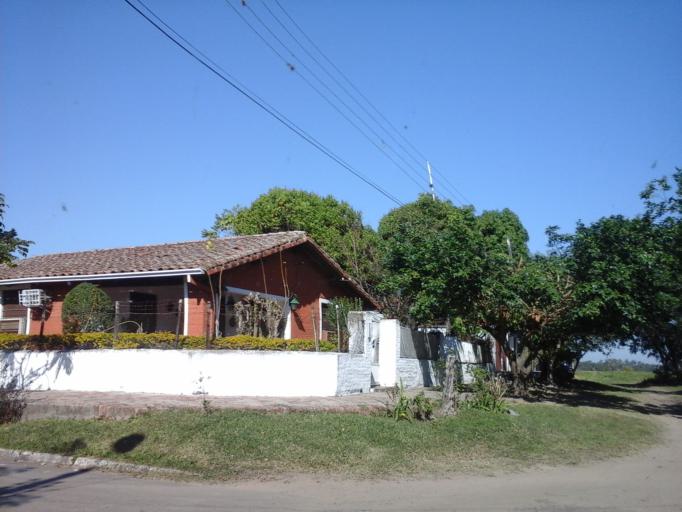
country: PY
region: Neembucu
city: Pilar
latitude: -26.8564
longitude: -58.3107
